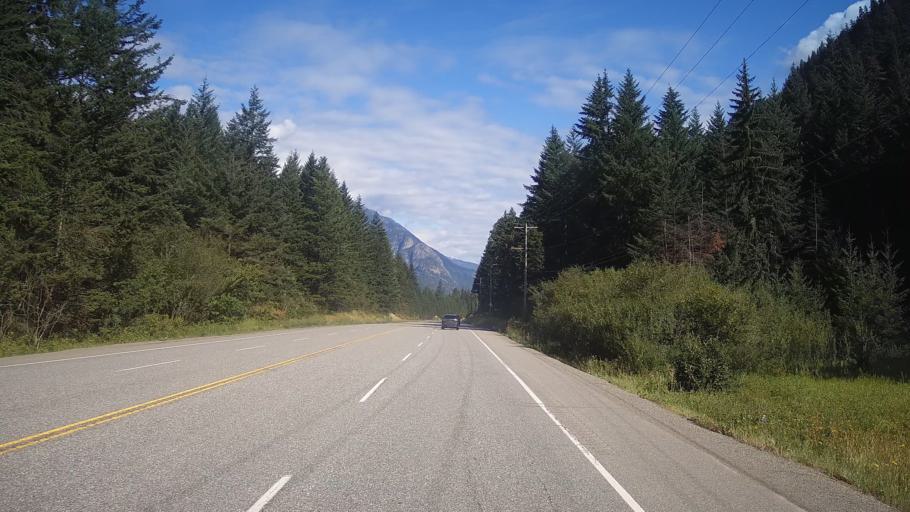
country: CA
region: British Columbia
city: Hope
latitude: 50.0448
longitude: -121.5381
